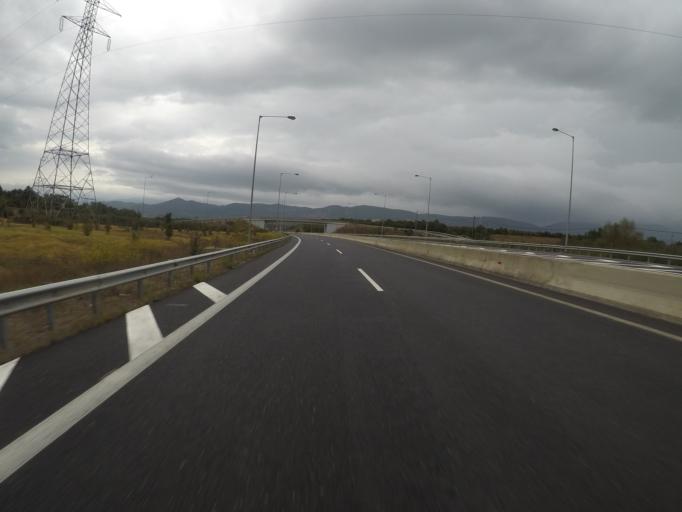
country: GR
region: Peloponnese
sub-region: Nomos Arkadias
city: Megalopoli
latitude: 37.3615
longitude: 22.1488
